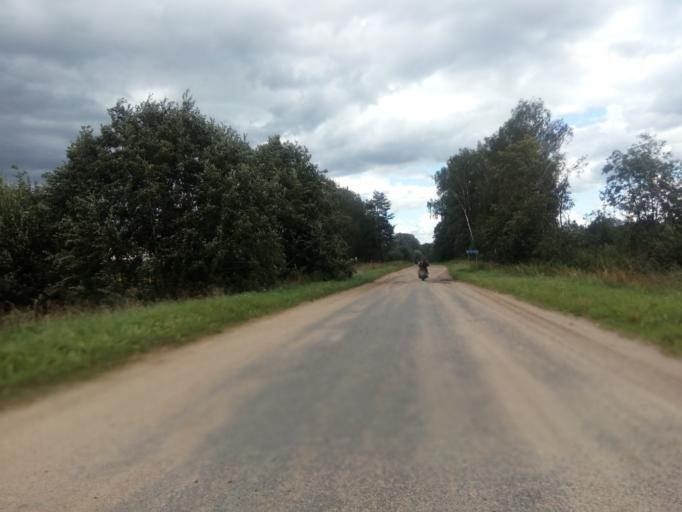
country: BY
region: Vitebsk
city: Dzisna
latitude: 55.7073
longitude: 28.3192
